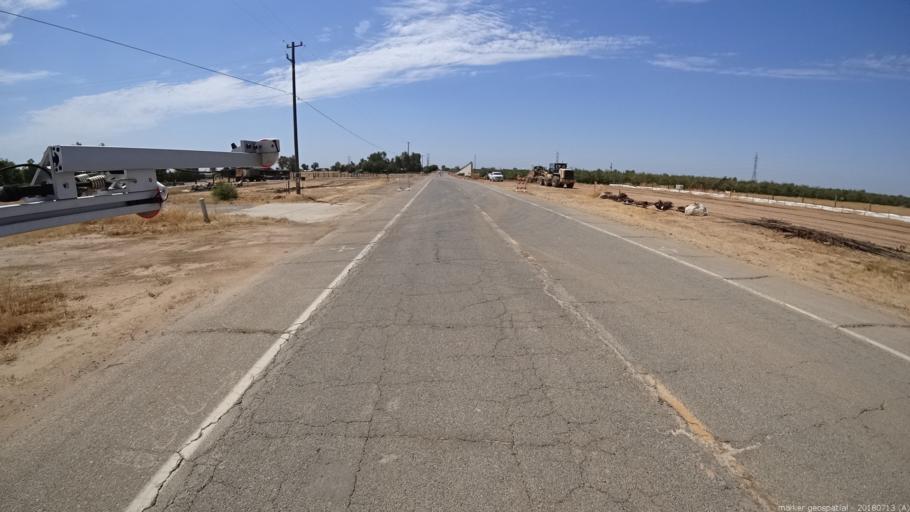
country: US
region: California
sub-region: Madera County
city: Madera Acres
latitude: 37.0043
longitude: -120.0562
